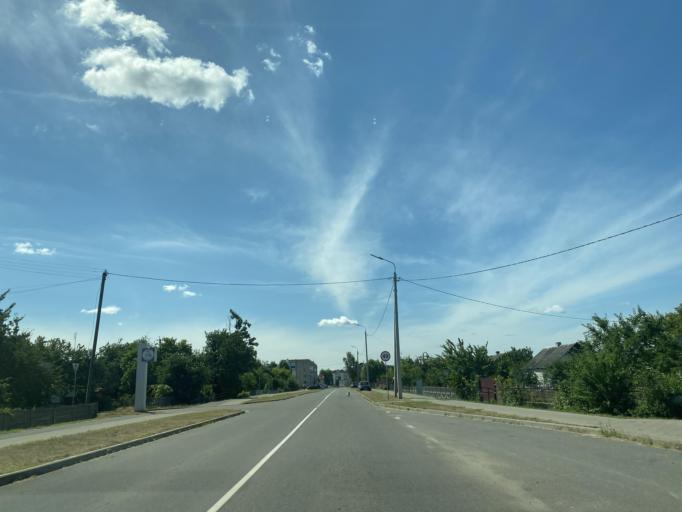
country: BY
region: Brest
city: Ivanava
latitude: 52.1541
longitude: 25.5437
